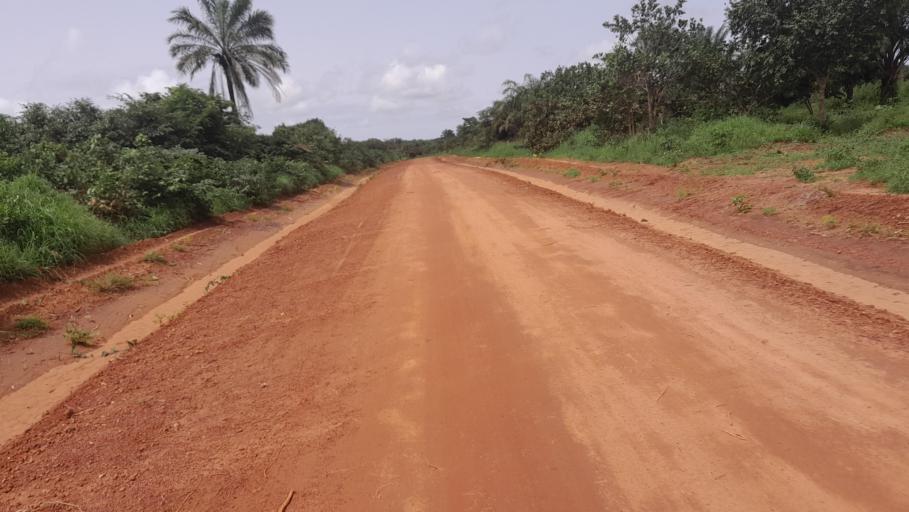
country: GN
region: Boke
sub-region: Boffa
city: Boffa
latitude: 10.0403
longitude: -13.8739
